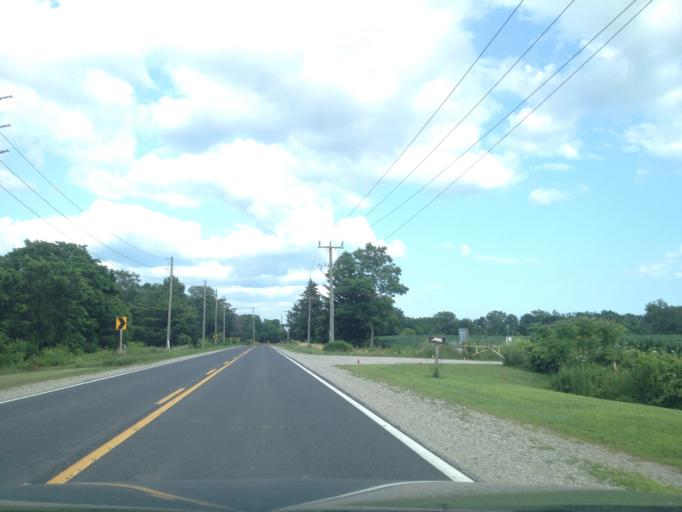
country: CA
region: Ontario
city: Aylmer
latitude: 42.6743
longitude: -80.9060
